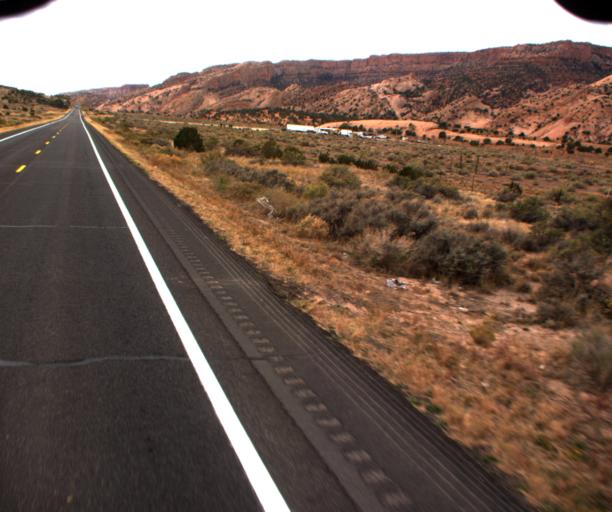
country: US
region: Arizona
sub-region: Navajo County
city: Kayenta
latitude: 36.6715
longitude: -110.4022
